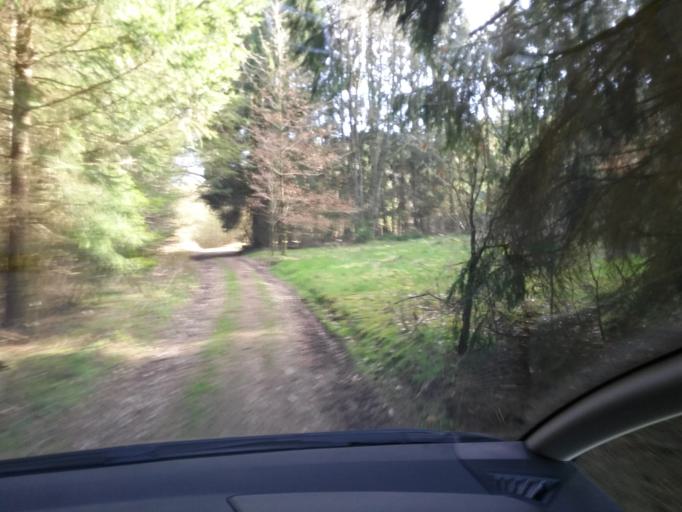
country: BE
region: Wallonia
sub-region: Province du Luxembourg
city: Daverdisse
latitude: 49.9893
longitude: 5.1592
